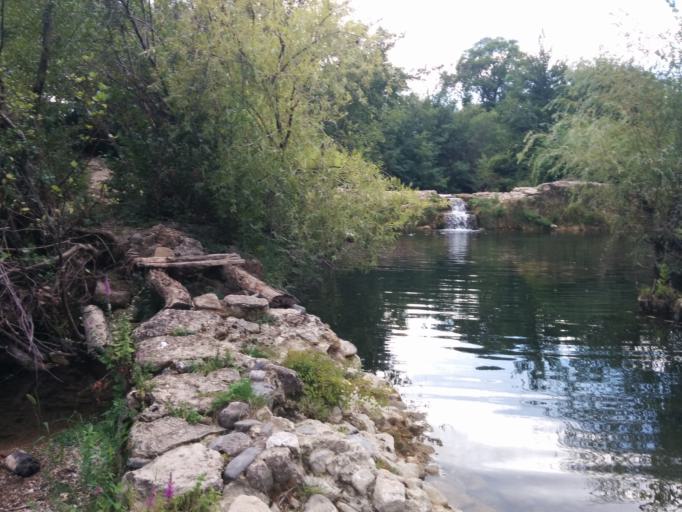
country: FR
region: Languedoc-Roussillon
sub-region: Departement du Gard
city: Saint-Christol-les-Ales
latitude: 44.0928
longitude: 4.0757
